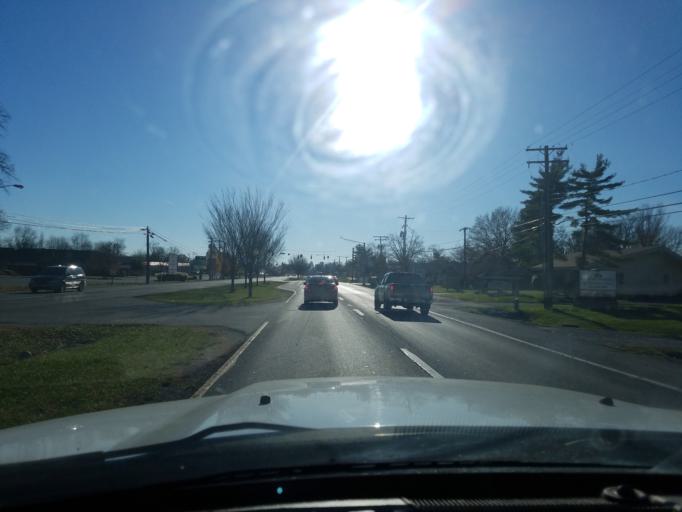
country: US
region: Indiana
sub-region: Clark County
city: Oak Park
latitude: 38.3058
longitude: -85.7220
